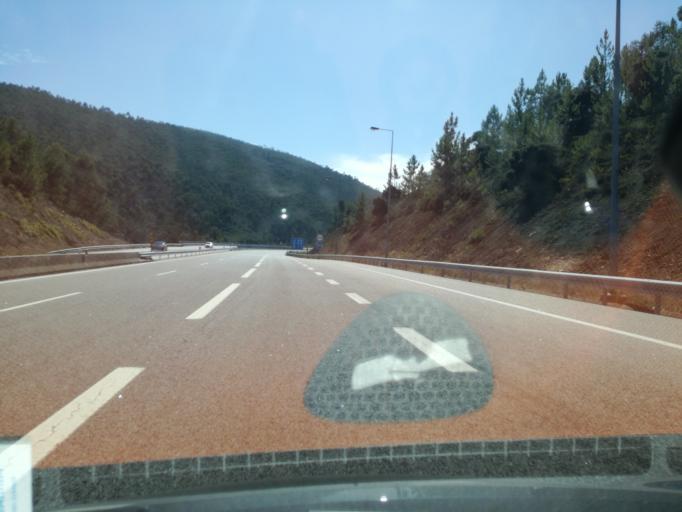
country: ES
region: Galicia
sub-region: Provincia de Pontevedra
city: O Rosal
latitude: 41.8759
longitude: -8.7865
